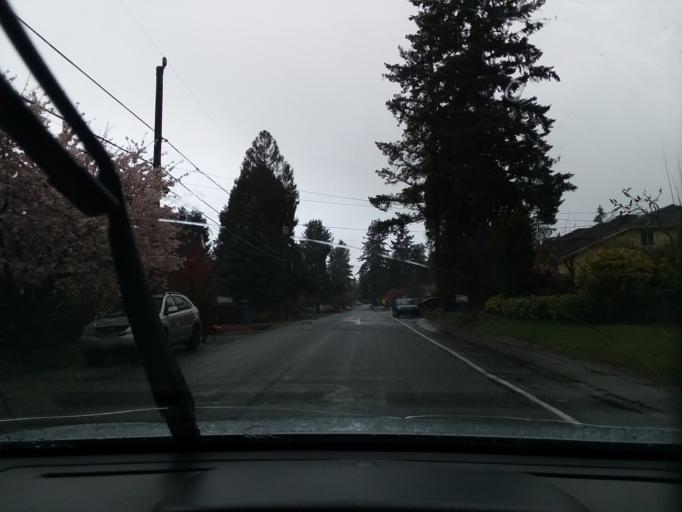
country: US
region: Washington
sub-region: King County
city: Shoreline
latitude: 47.7452
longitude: -122.3157
